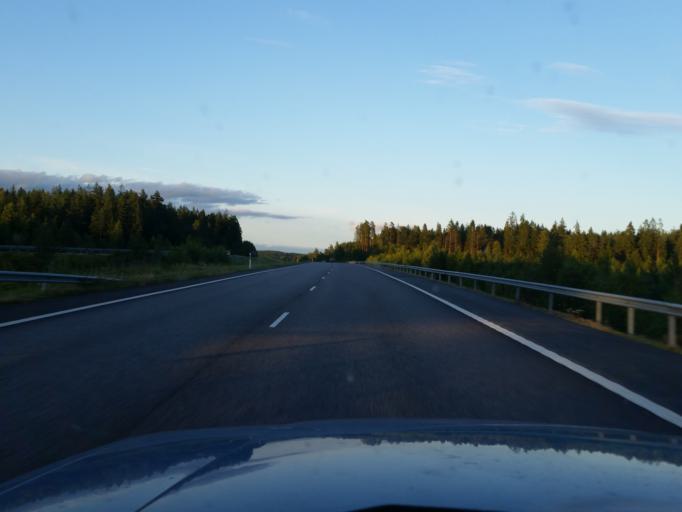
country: FI
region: Varsinais-Suomi
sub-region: Loimaa
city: Marttila
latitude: 60.4286
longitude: 22.8905
